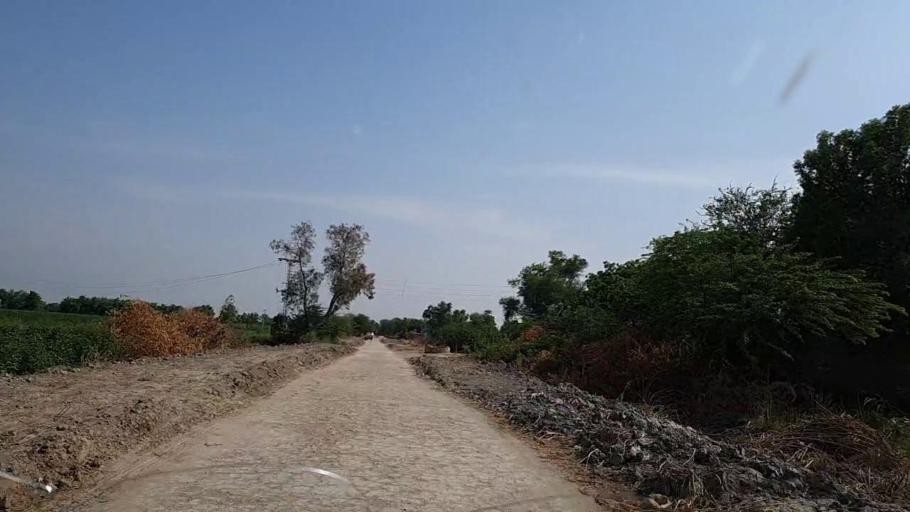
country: PK
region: Sindh
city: Khanpur
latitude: 27.7469
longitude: 69.3412
